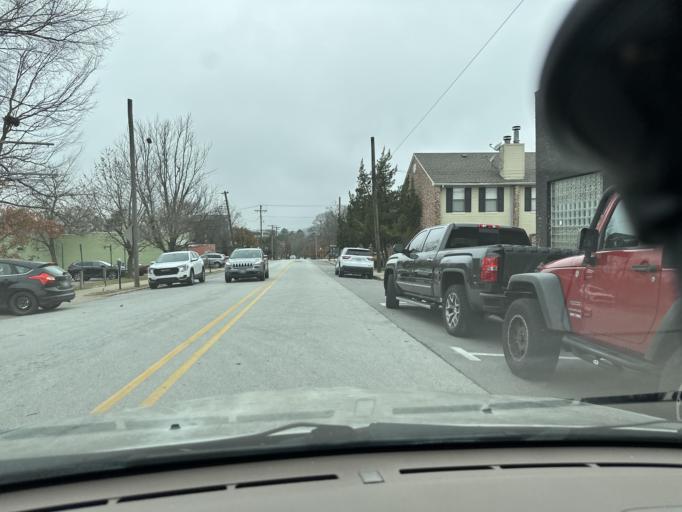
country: US
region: Arkansas
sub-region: Washington County
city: Fayetteville
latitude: 36.0620
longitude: -94.1621
